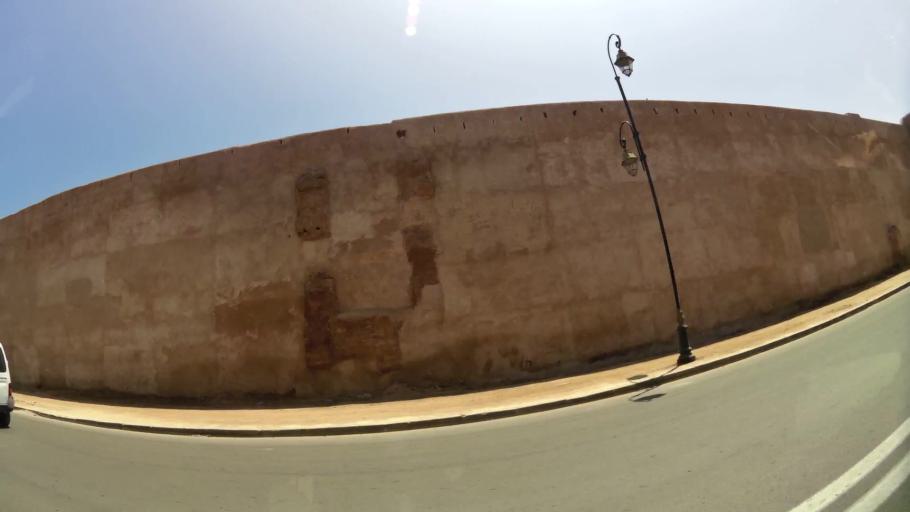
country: MA
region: Rabat-Sale-Zemmour-Zaer
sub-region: Rabat
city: Rabat
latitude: 34.0258
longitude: -6.8413
